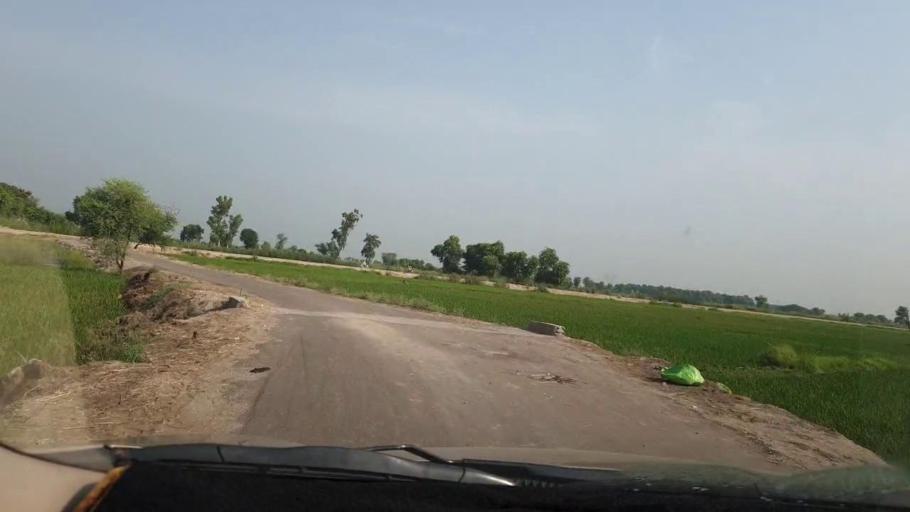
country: PK
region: Sindh
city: Goth Garelo
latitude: 27.4721
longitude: 68.0787
